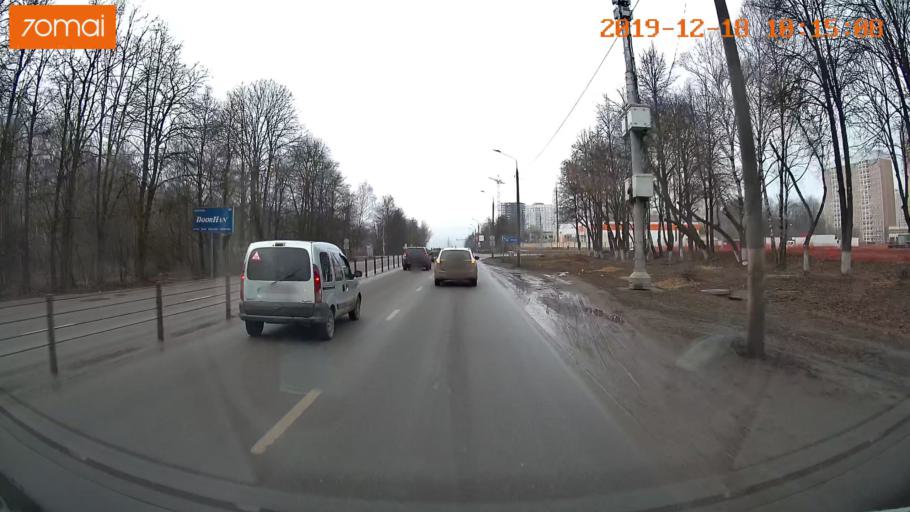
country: RU
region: Moskovskaya
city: Dubrovitsy
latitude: 55.4124
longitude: 37.4849
